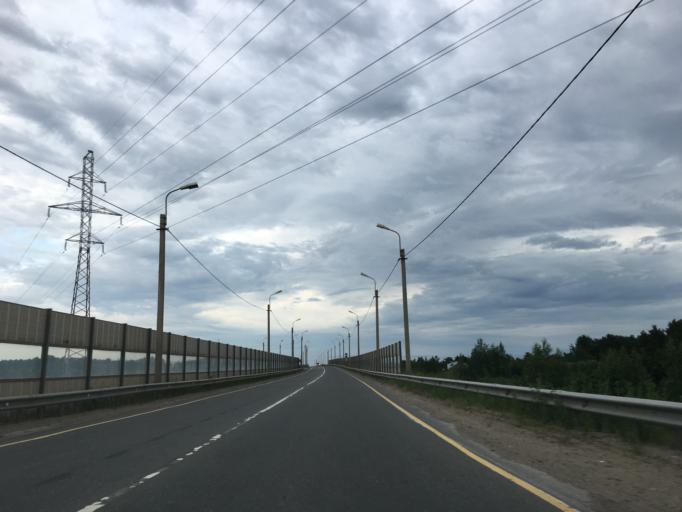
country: RU
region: Pskov
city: Pskov
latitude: 57.8353
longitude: 28.4157
